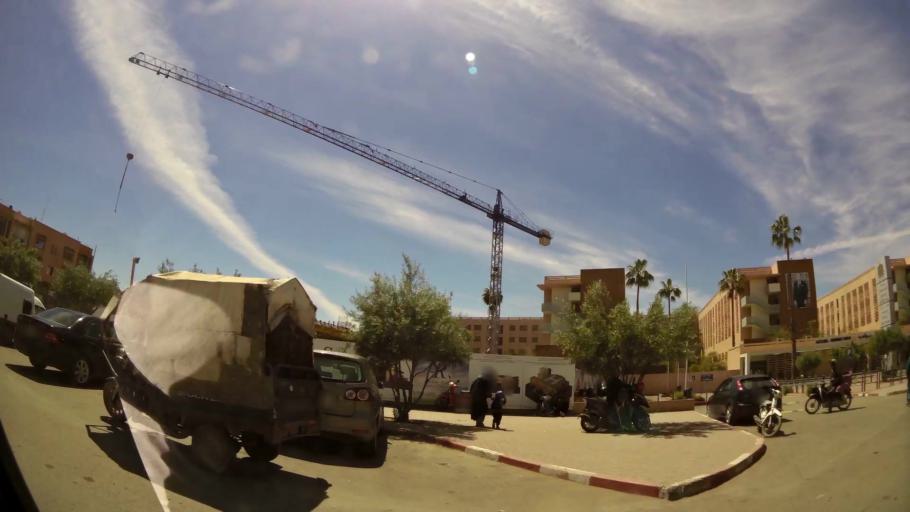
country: MA
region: Marrakech-Tensift-Al Haouz
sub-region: Marrakech
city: Marrakesh
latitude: 31.6631
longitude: -7.9938
